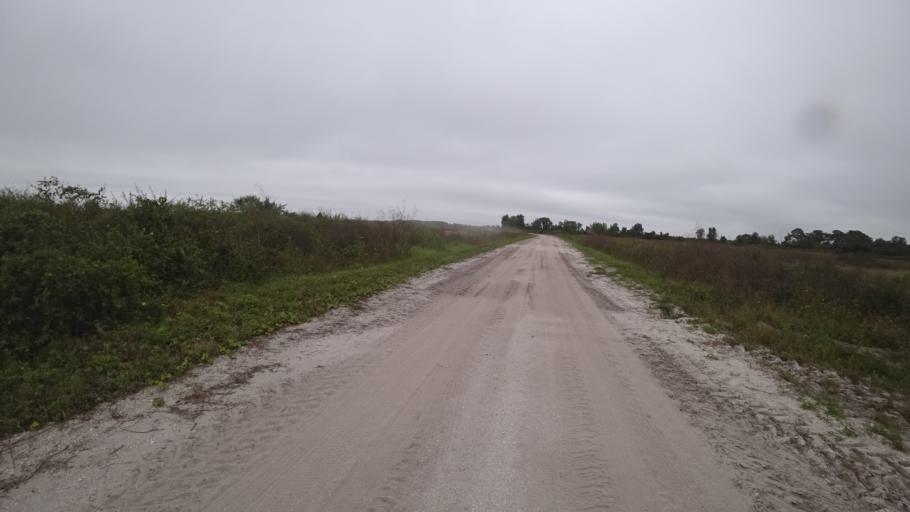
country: US
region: Florida
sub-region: Sarasota County
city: Warm Mineral Springs
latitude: 27.2927
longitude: -82.1346
